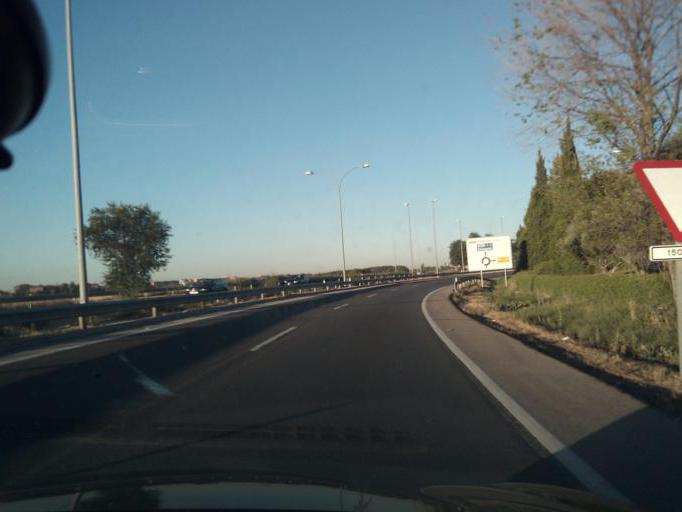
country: ES
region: Madrid
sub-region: Provincia de Madrid
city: Torrejon de Ardoz
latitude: 40.4749
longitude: -3.4775
